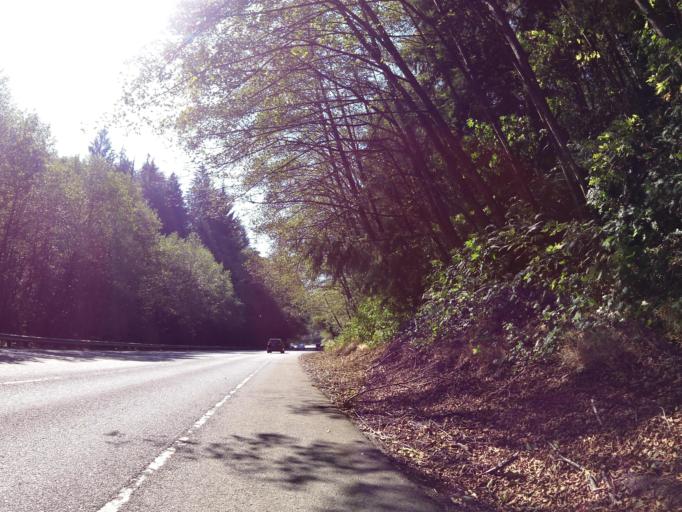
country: US
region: Oregon
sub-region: Clatsop County
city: Cannon Beach
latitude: 45.9227
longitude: -123.9335
